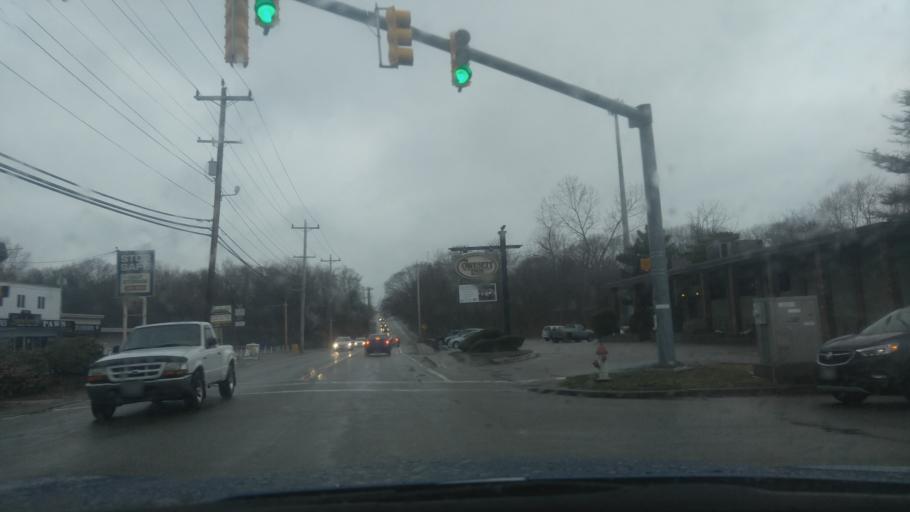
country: US
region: Rhode Island
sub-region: Kent County
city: West Warwick
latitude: 41.6849
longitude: -71.5093
